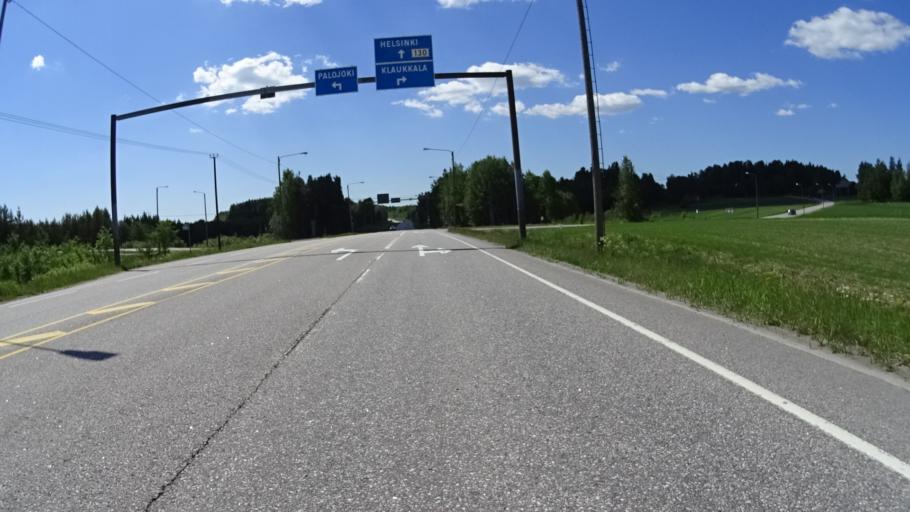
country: FI
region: Uusimaa
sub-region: Helsinki
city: Nurmijaervi
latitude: 60.3965
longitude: 24.8134
